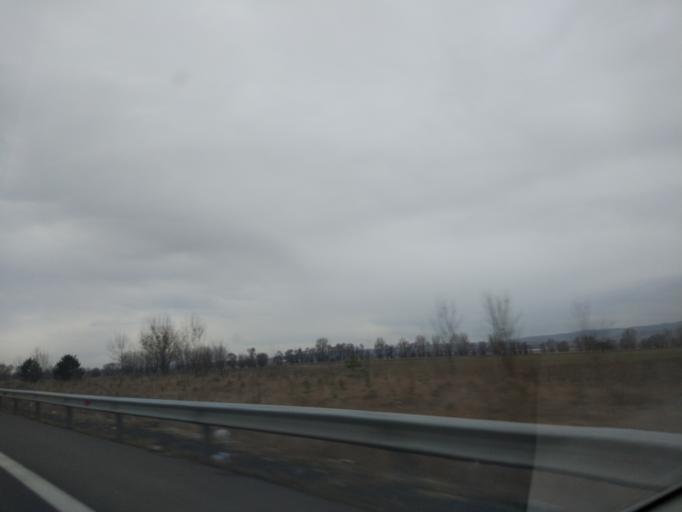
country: TR
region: Bolu
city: Gerede
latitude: 40.7394
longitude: 32.1884
